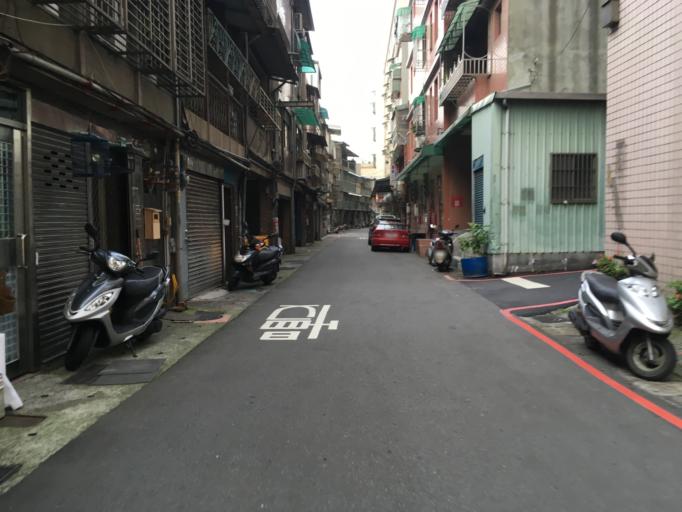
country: TW
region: Taiwan
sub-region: Taoyuan
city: Taoyuan
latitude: 24.9315
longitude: 121.3696
